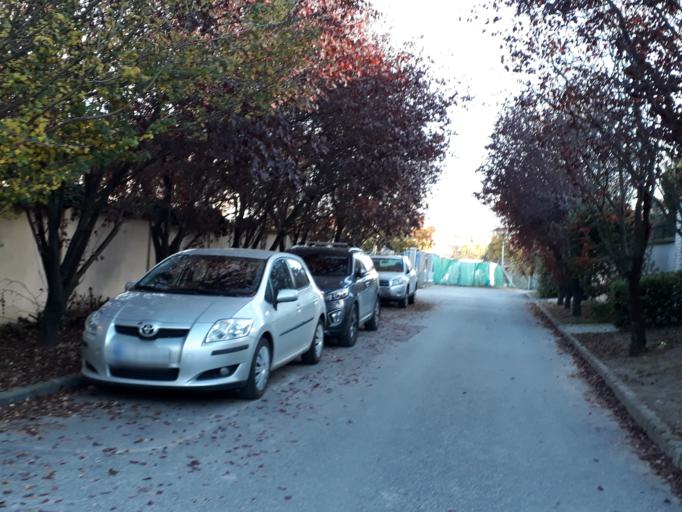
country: HU
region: Budapest
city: Budapest XII. keruelet
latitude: 47.4760
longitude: 18.9945
